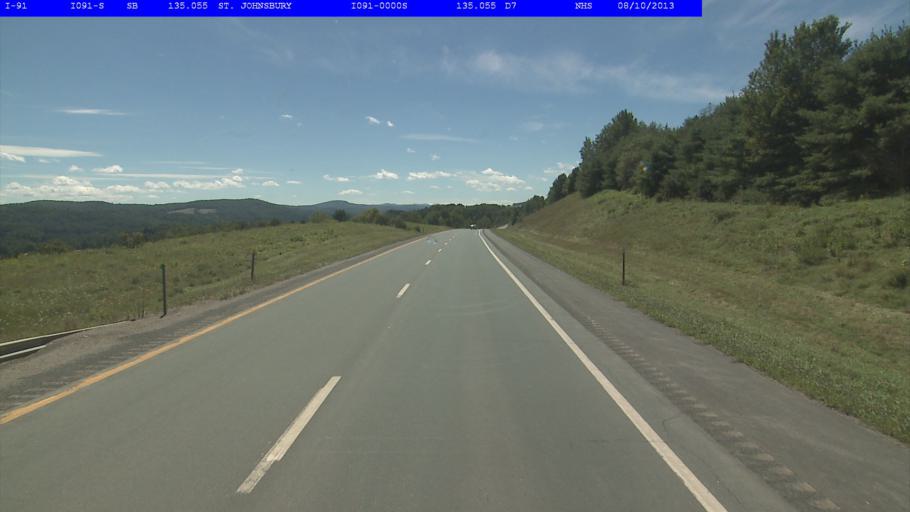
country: US
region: Vermont
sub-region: Caledonia County
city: Lyndon
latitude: 44.4902
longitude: -72.0222
